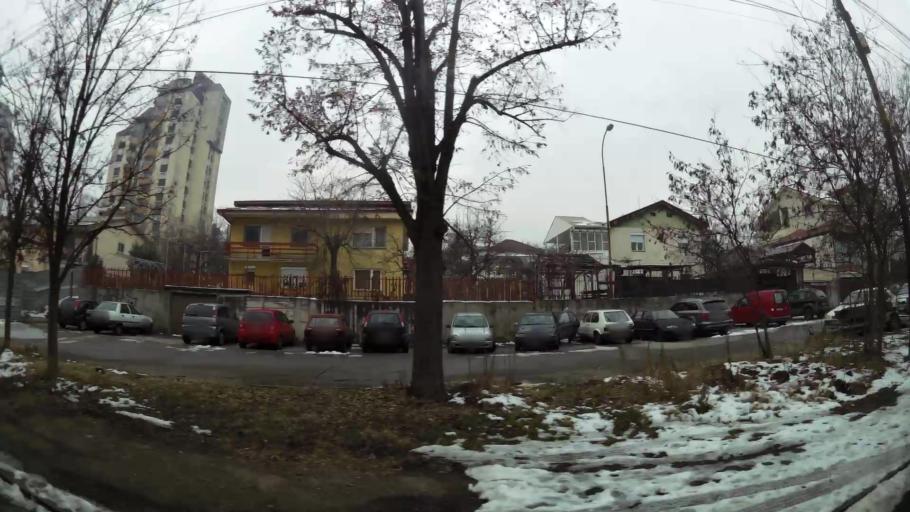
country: MK
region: Cair
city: Cair
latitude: 42.0119
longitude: 21.4604
